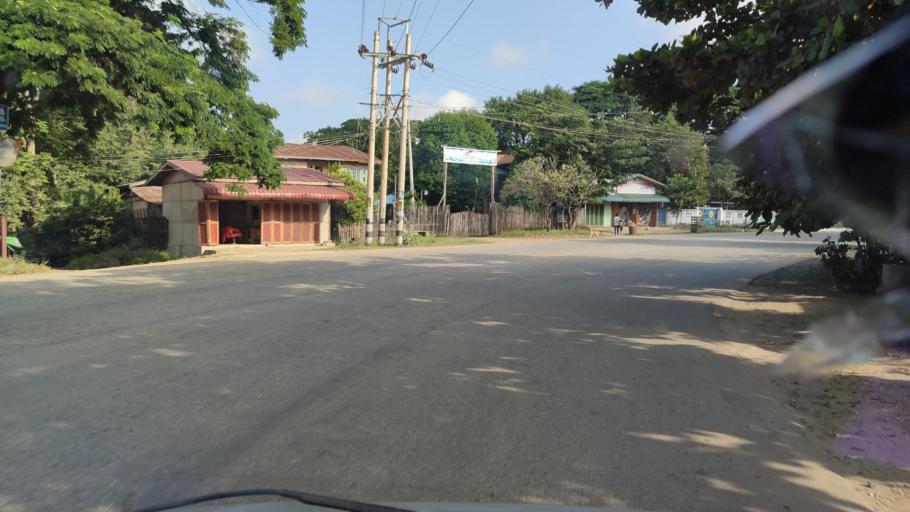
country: MM
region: Mandalay
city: Yamethin
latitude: 20.7605
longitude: 96.3178
